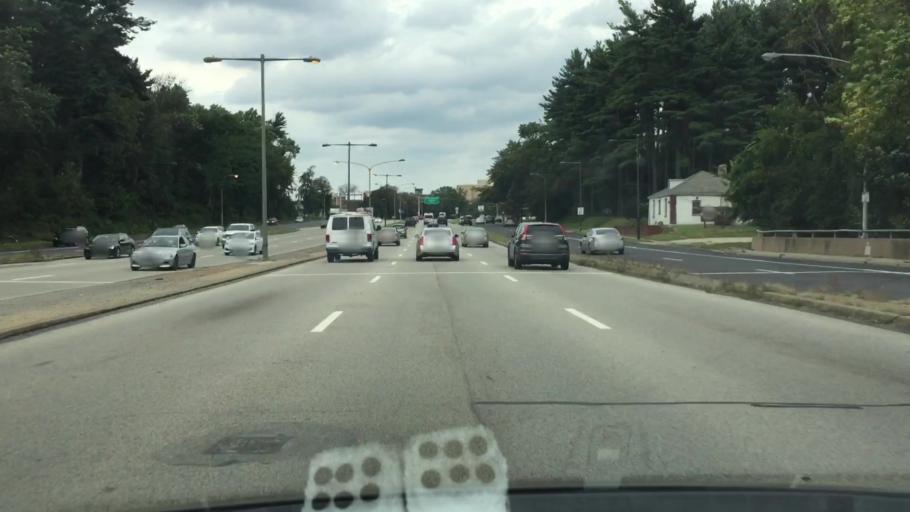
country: US
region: Pennsylvania
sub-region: Montgomery County
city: Rockledge
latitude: 40.0663
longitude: -75.0410
